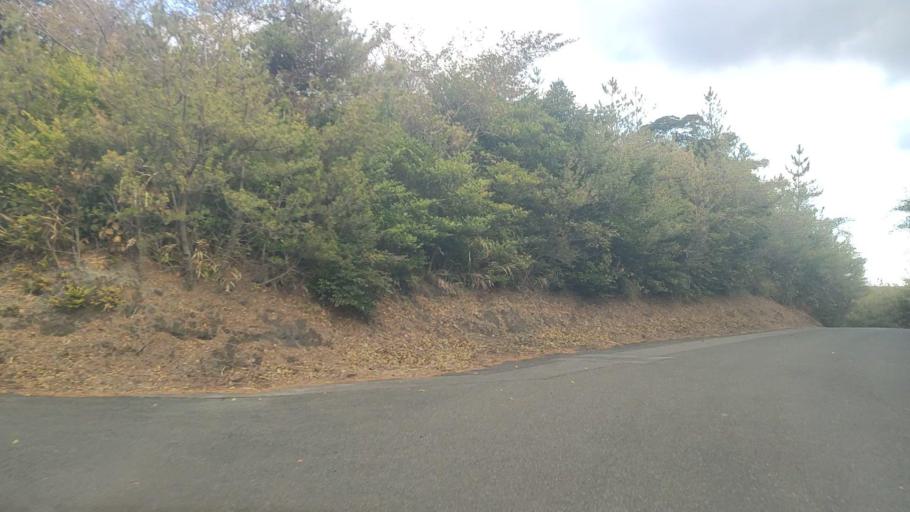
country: JP
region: Kagoshima
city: Kagoshima-shi
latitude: 31.5928
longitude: 130.6349
